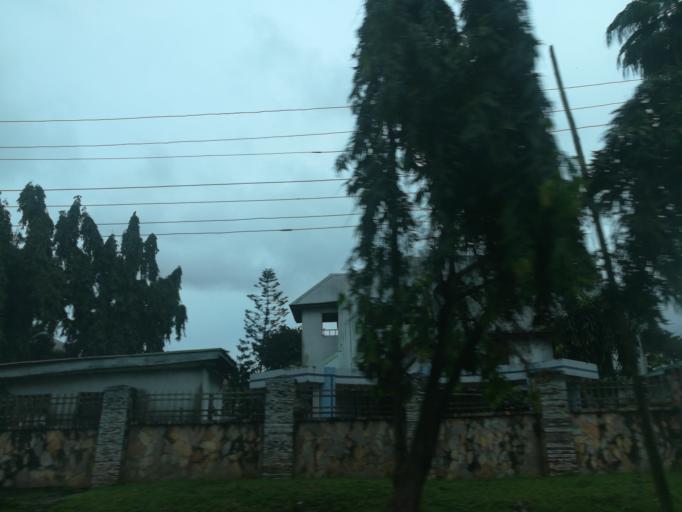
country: NG
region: Rivers
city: Port Harcourt
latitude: 4.8171
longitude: 7.0001
